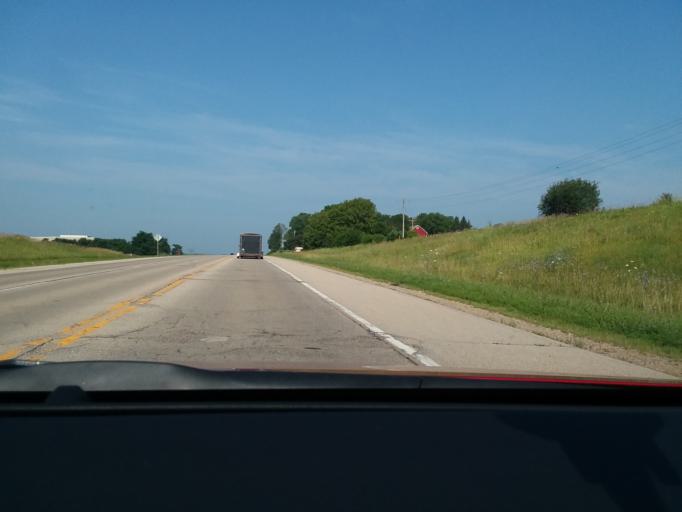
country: US
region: Wisconsin
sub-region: Dane County
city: Waunakee
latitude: 43.1919
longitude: -89.4287
